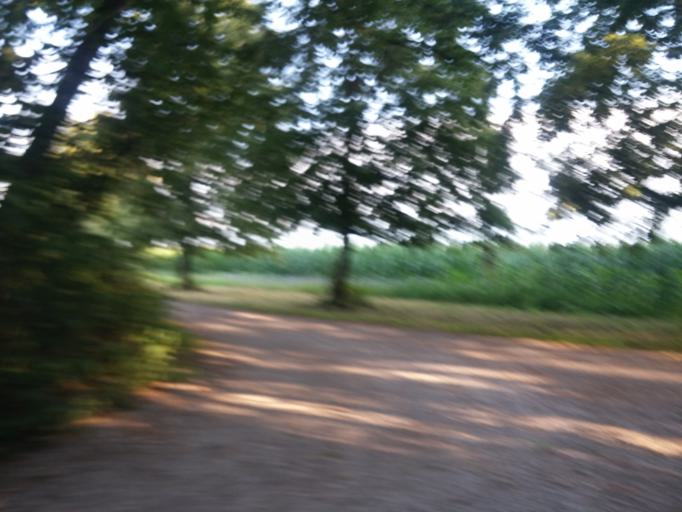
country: DE
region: Bavaria
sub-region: Upper Bavaria
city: Grasbrunn
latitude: 48.0637
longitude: 11.7609
